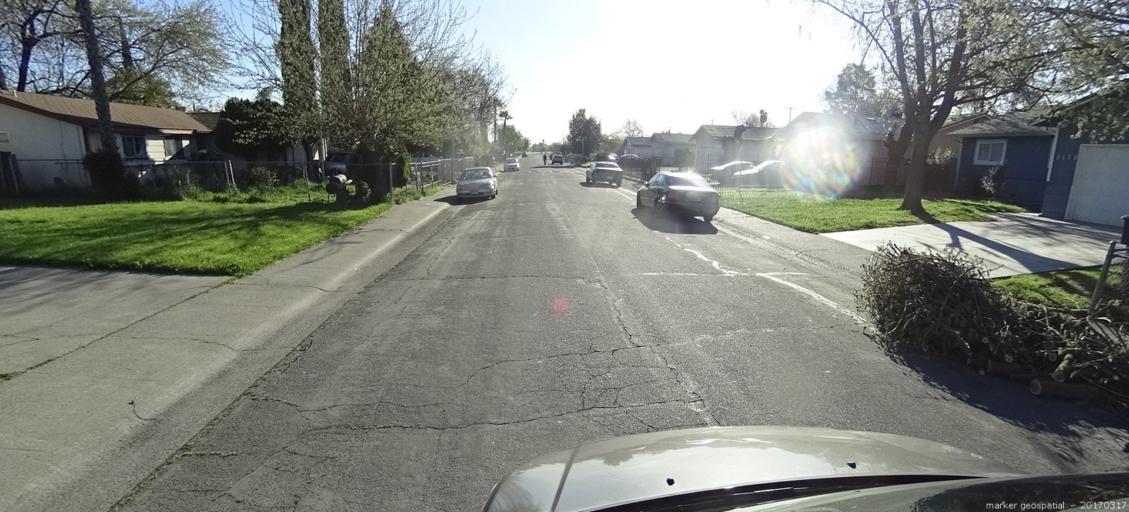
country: US
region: California
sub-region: Sacramento County
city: Parkway
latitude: 38.4881
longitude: -121.4913
